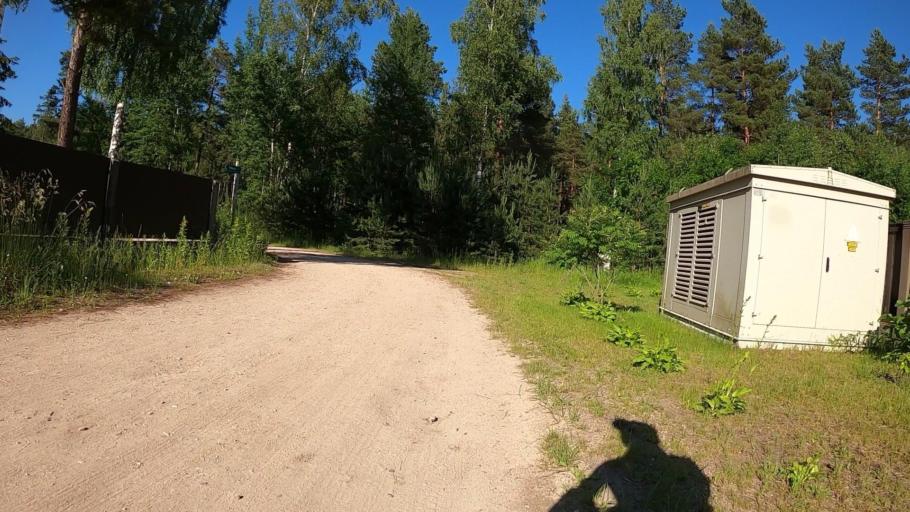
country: LV
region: Stopini
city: Ulbroka
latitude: 56.8783
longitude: 24.3000
